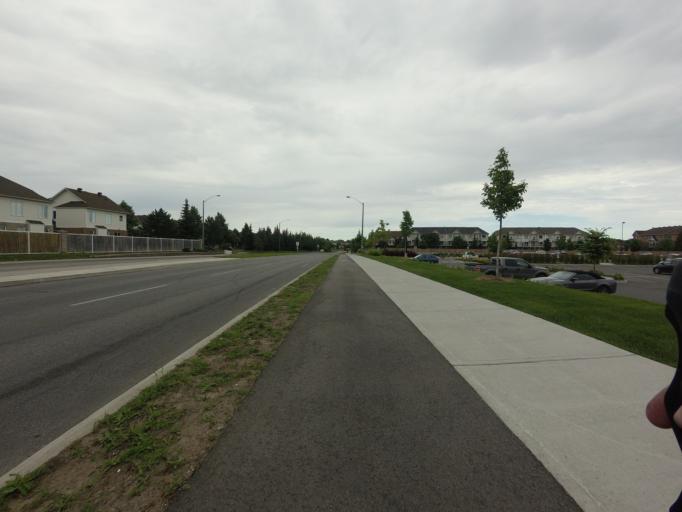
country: CA
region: Ontario
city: Bells Corners
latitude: 45.2768
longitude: -75.7154
